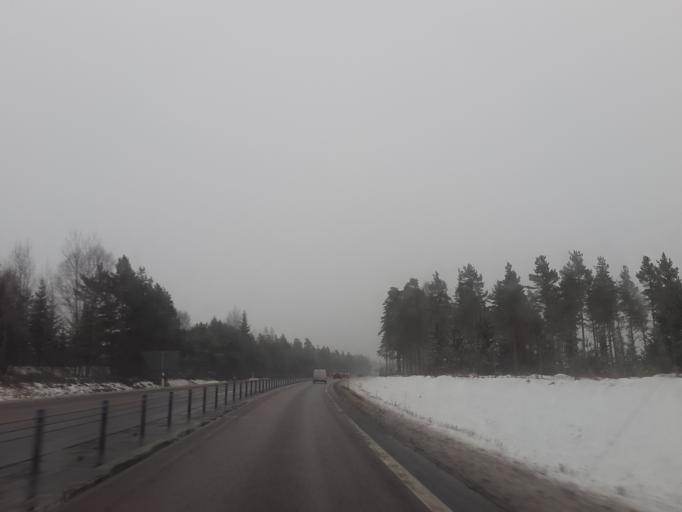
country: SE
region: Joenkoeping
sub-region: Jonkopings Kommun
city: Jonkoping
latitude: 57.7720
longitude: 14.0815
